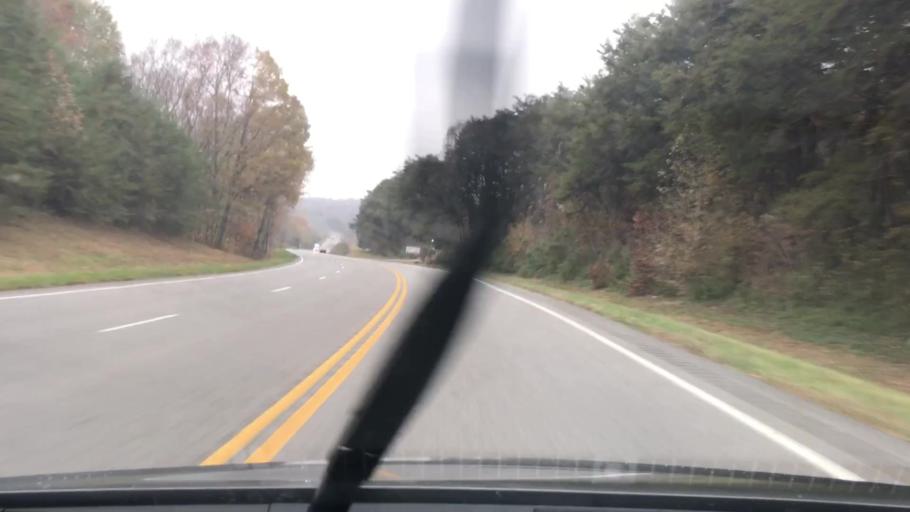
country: US
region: Kentucky
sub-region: Barren County
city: Glasgow
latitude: 36.8695
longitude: -86.0339
